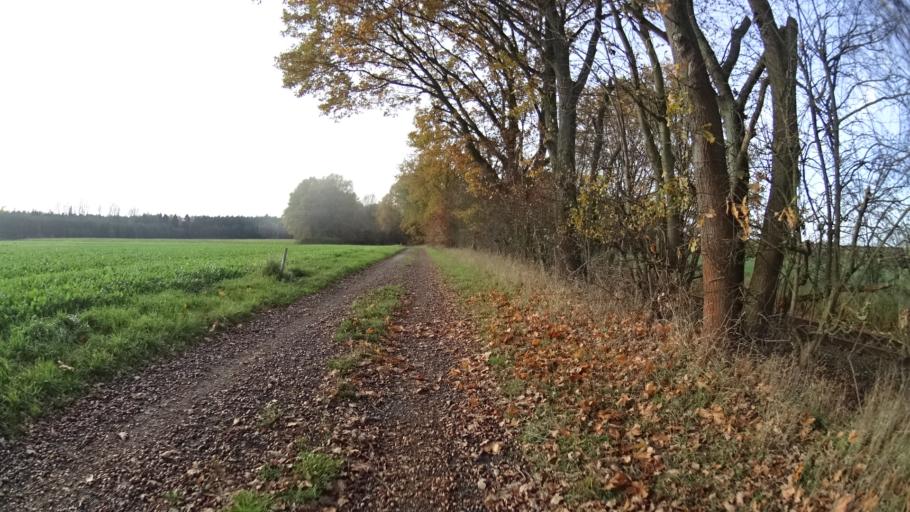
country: DE
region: Lower Saxony
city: Wendisch Evern
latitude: 53.2182
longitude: 10.4550
